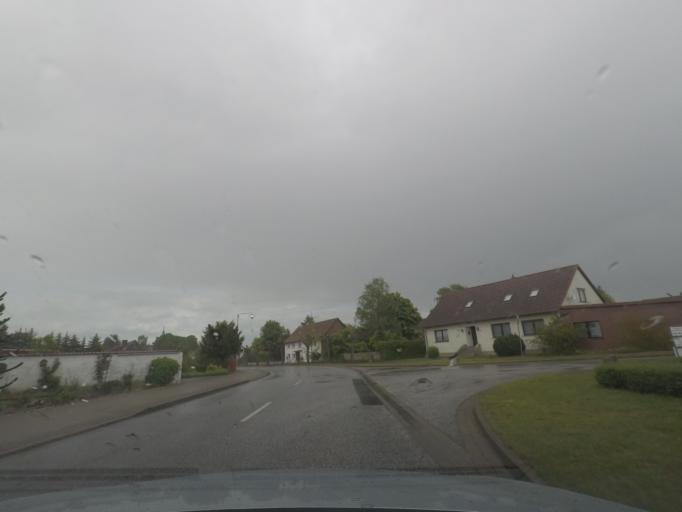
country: DE
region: Saxony-Anhalt
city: Kusey
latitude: 52.5784
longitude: 11.0910
